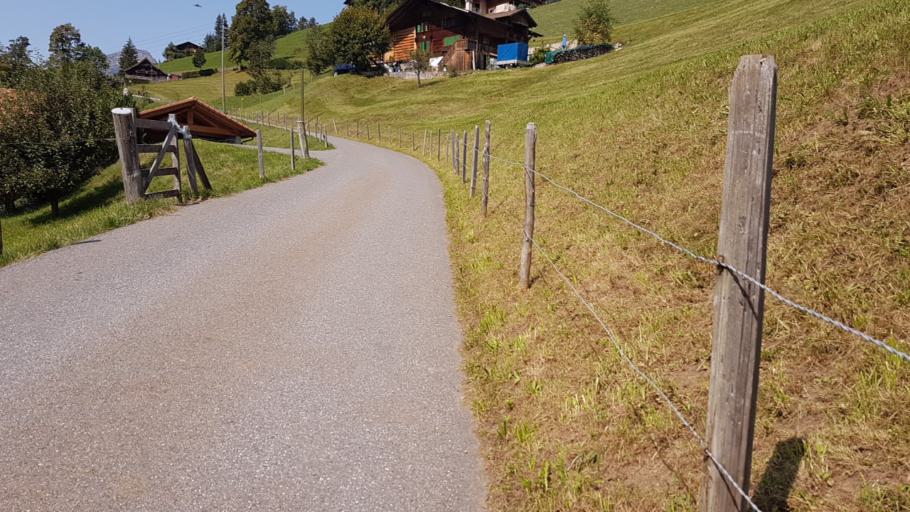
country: CH
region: Bern
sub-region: Frutigen-Niedersimmental District
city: Aeschi
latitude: 46.5922
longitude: 7.7186
